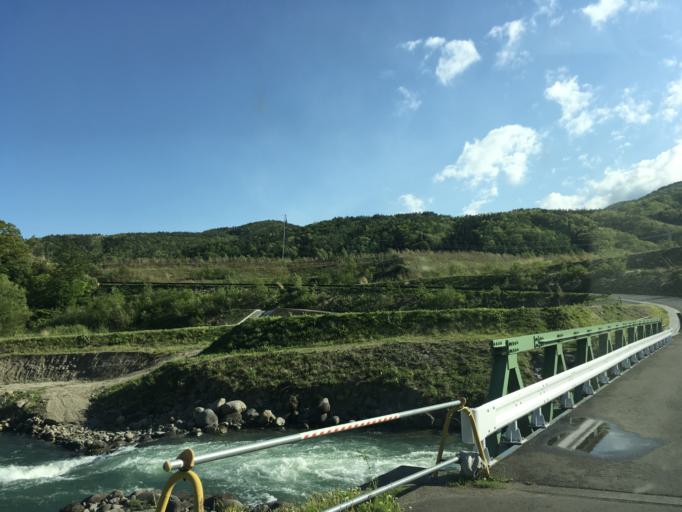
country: JP
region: Iwate
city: Mizusawa
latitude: 39.1235
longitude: 140.9323
